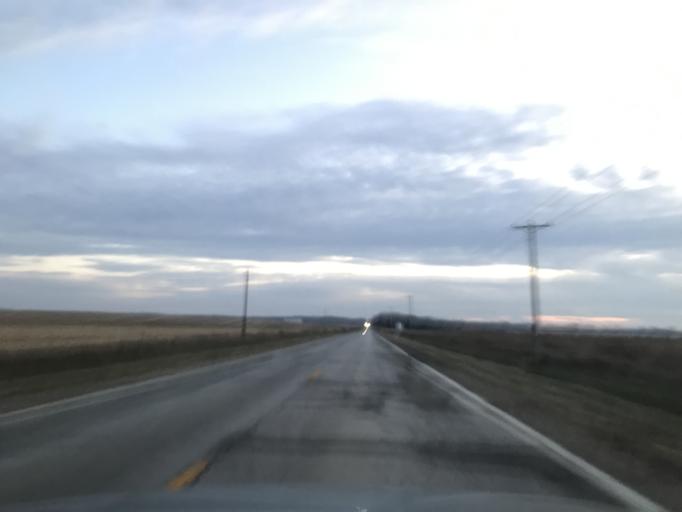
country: US
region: Iowa
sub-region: Des Moines County
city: Burlington
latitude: 40.7016
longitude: -91.0701
